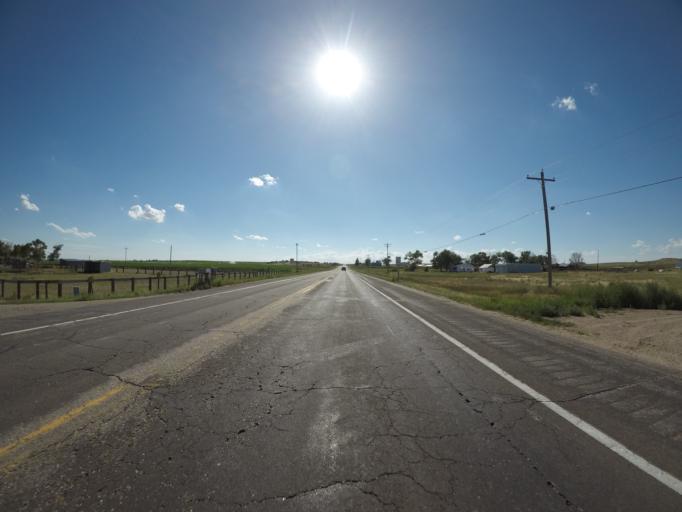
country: US
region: Colorado
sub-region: Logan County
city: Sterling
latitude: 40.6238
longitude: -103.3048
